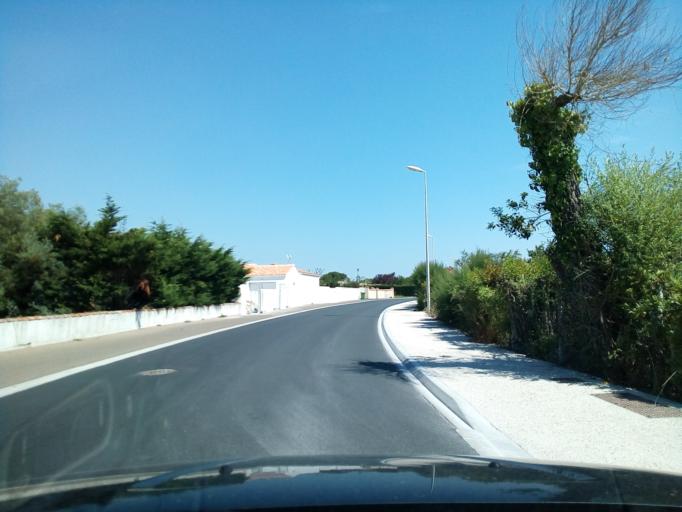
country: FR
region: Poitou-Charentes
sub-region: Departement de la Charente-Maritime
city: Boyard-Ville
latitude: 45.9740
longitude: -1.2987
